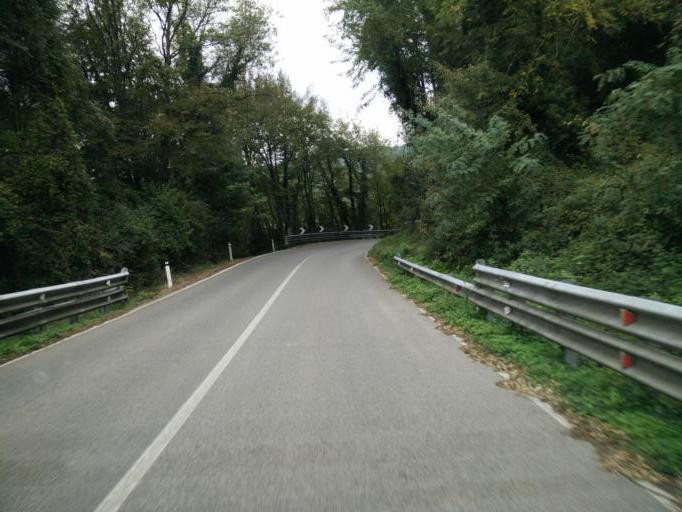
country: IT
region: Tuscany
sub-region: Provincia di Massa-Carrara
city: Fivizzano
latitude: 44.2152
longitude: 10.0920
